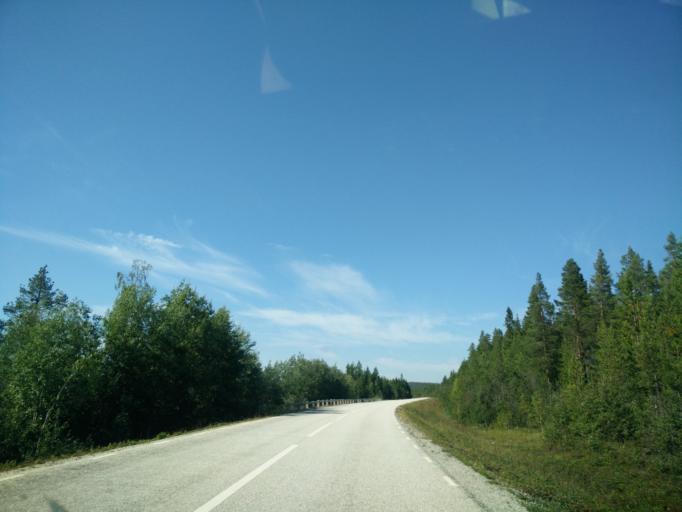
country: SE
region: Jaemtland
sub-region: Are Kommun
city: Jarpen
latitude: 62.8110
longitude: 13.5245
